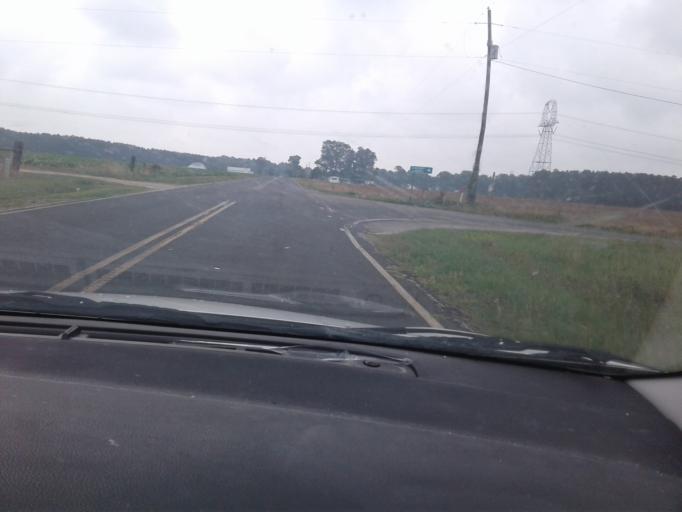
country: US
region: North Carolina
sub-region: Harnett County
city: Coats
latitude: 35.3762
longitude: -78.6476
